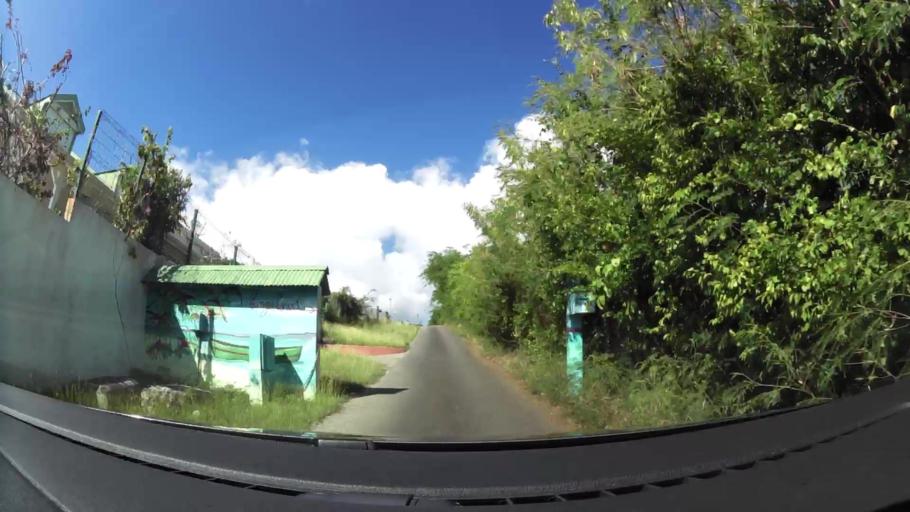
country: GP
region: Guadeloupe
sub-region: Guadeloupe
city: Sainte-Anne
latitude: 16.2352
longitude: -61.3772
